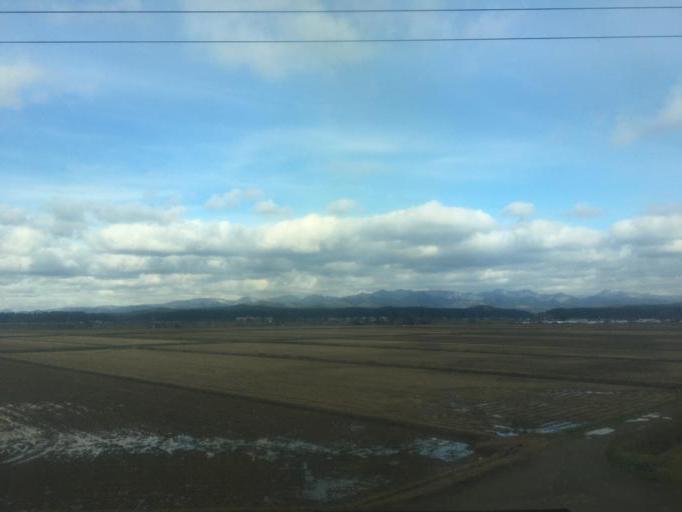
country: JP
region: Akita
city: Noshiromachi
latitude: 40.2122
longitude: 140.1412
